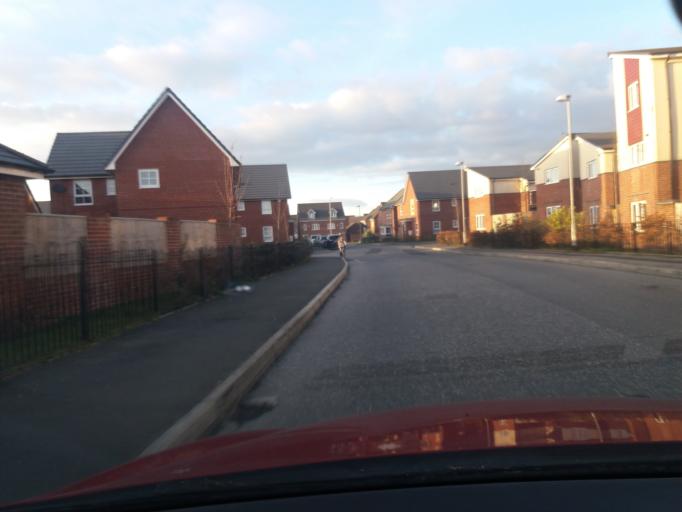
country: GB
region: England
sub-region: Lancashire
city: Euxton
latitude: 53.6759
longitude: -2.6606
